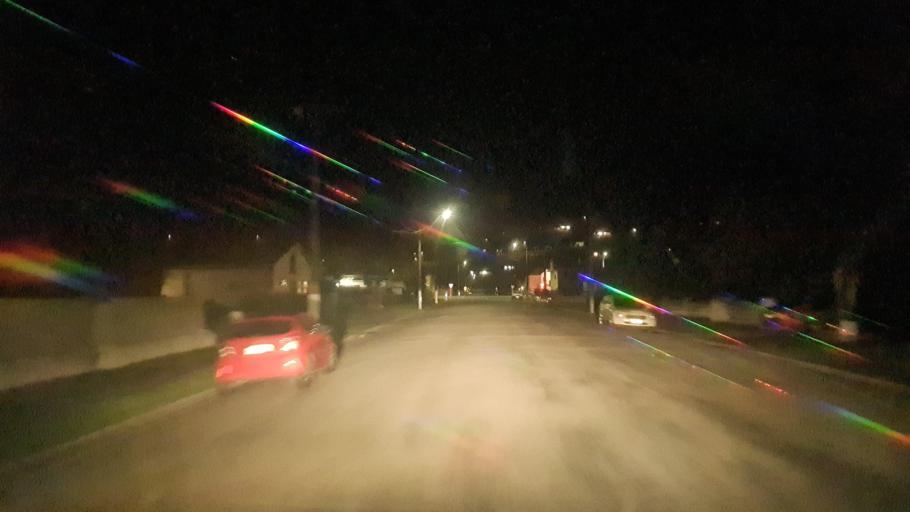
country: NZ
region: Otago
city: Oamaru
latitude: -45.0920
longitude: 170.9760
